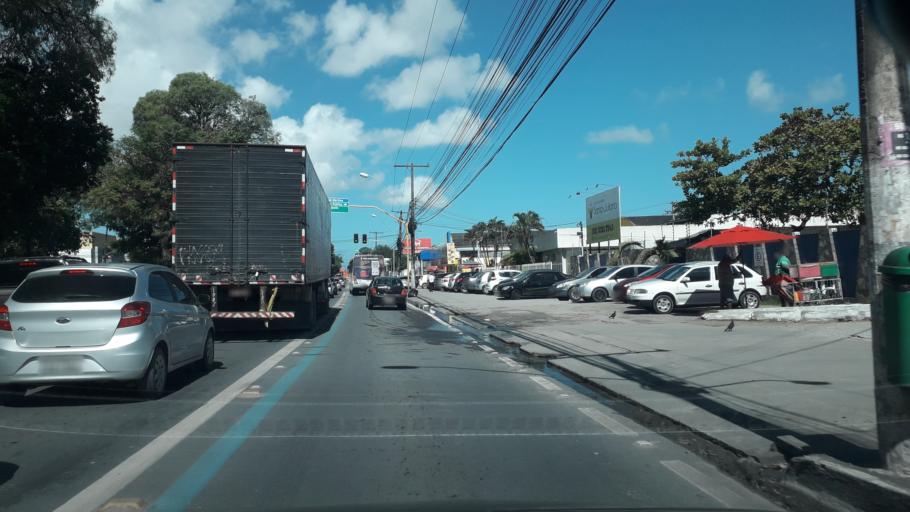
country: BR
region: Alagoas
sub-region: Satuba
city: Satuba
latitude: -9.5860
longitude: -35.7635
